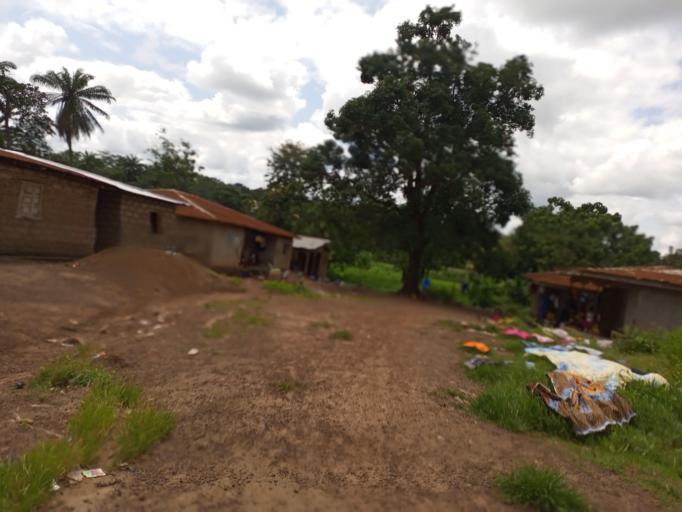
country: SL
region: Northern Province
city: Kamakwie
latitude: 9.4979
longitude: -12.2445
